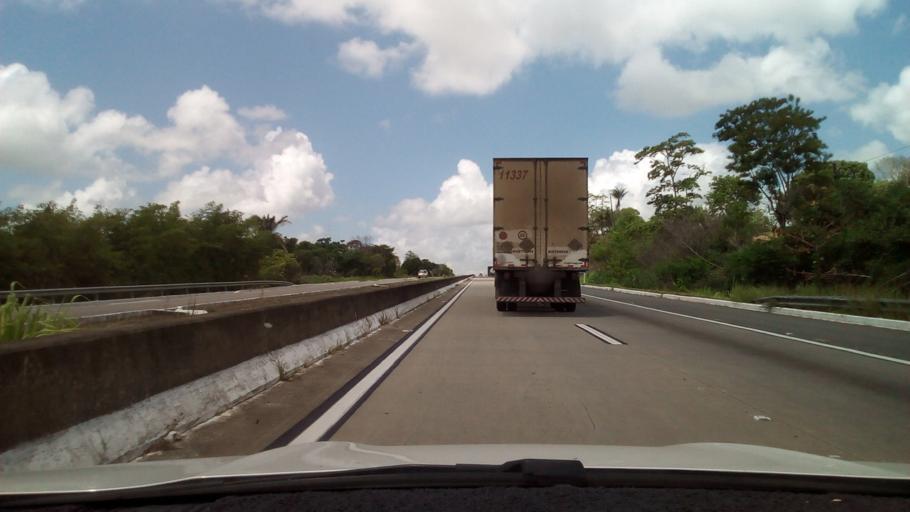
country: BR
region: Paraiba
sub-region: Alhandra
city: Alhandra
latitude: -7.3677
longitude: -34.9535
